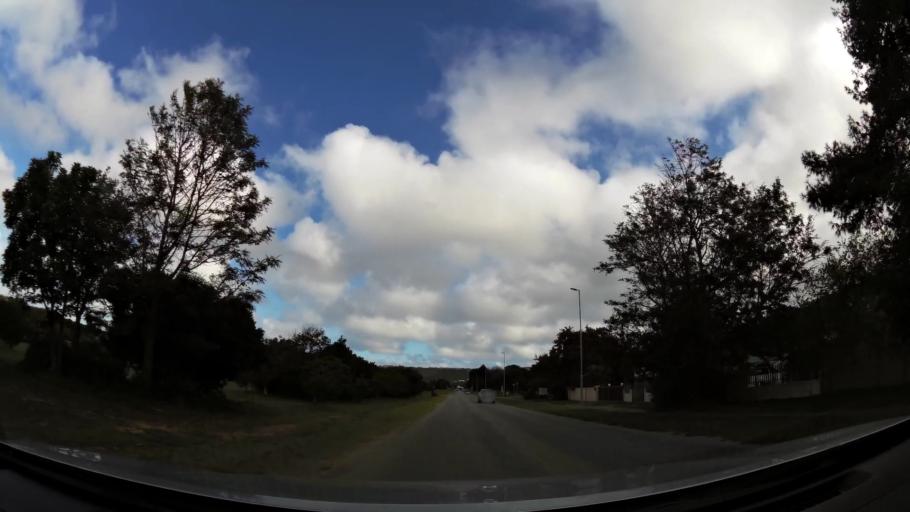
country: ZA
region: Western Cape
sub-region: Eden District Municipality
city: Plettenberg Bay
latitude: -34.0711
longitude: 23.3683
